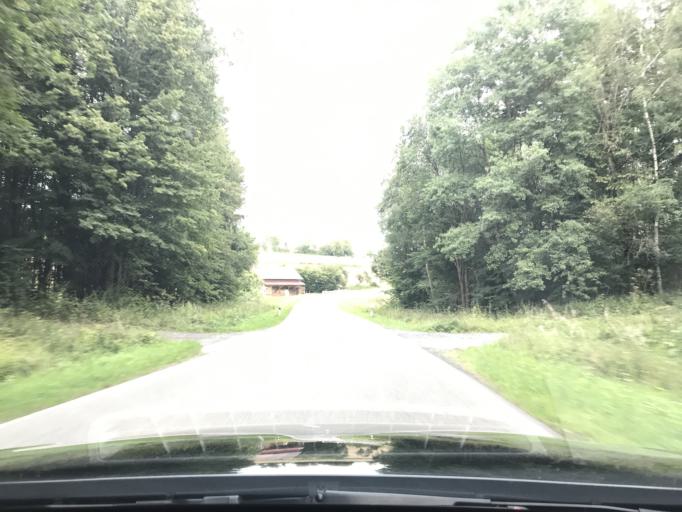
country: DE
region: Bavaria
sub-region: Regierungsbezirk Unterfranken
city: Breitbrunn
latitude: 50.0412
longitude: 10.6524
